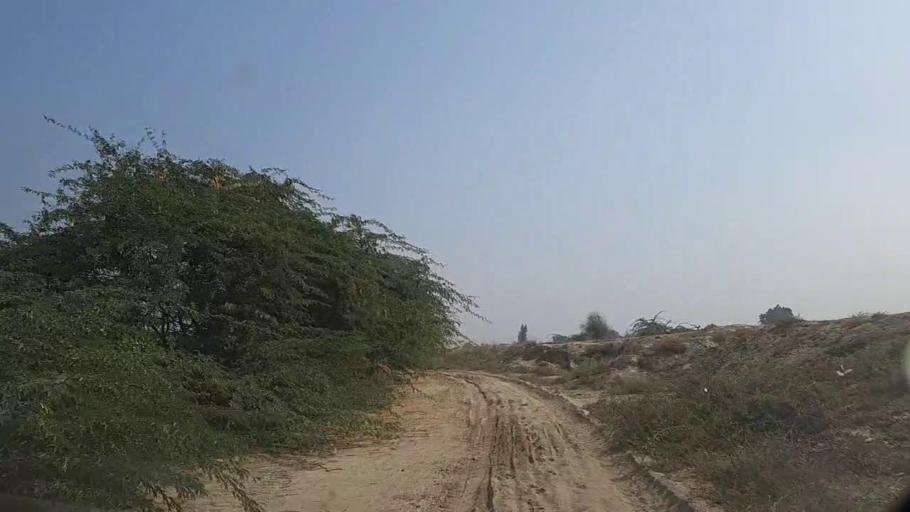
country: PK
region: Sindh
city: Thatta
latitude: 24.6535
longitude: 67.9235
